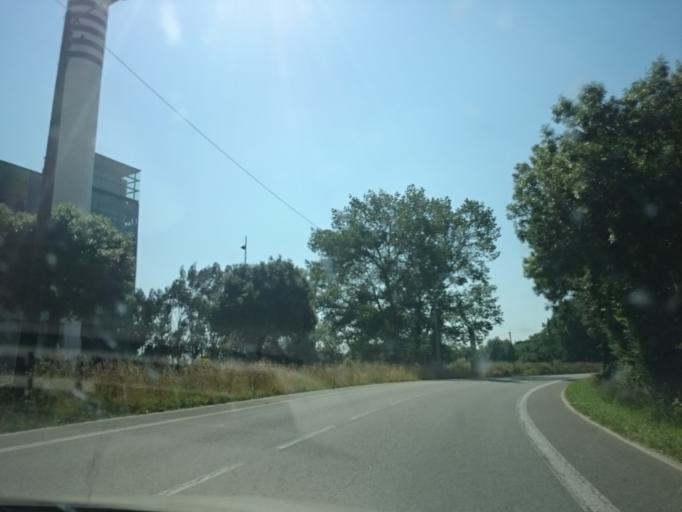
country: FR
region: Pays de la Loire
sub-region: Departement de la Loire-Atlantique
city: Coueron
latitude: 47.2094
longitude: -1.7068
